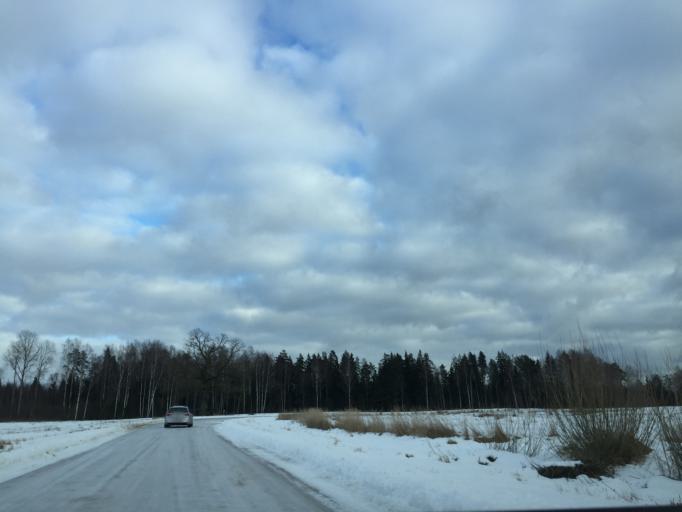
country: LV
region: Lielvarde
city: Lielvarde
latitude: 56.5839
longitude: 24.7373
